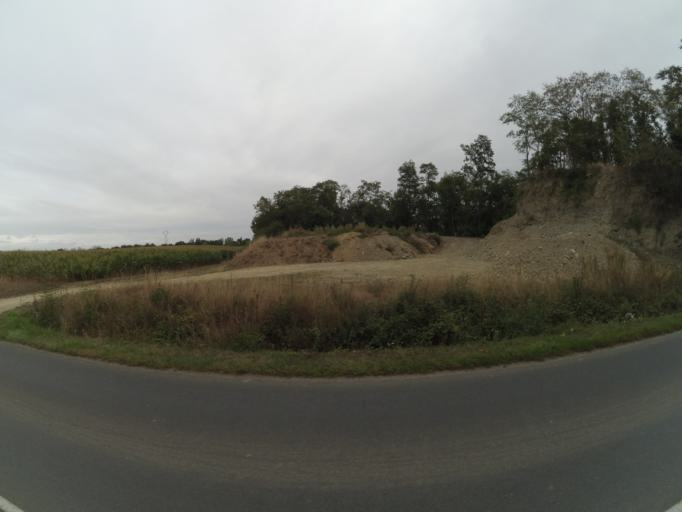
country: FR
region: Pays de la Loire
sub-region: Departement de la Vendee
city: Saint-Andre-Treize-Voies
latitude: 46.9233
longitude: -1.3955
